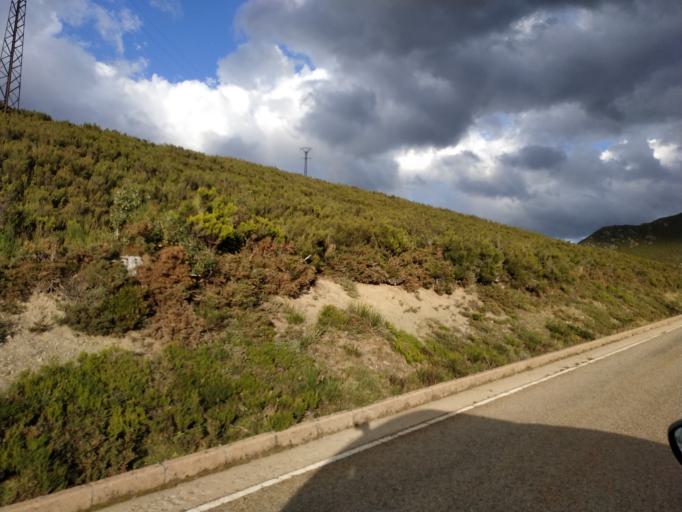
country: ES
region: Castille and Leon
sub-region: Provincia de Leon
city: Candin
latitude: 42.8741
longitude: -6.8262
